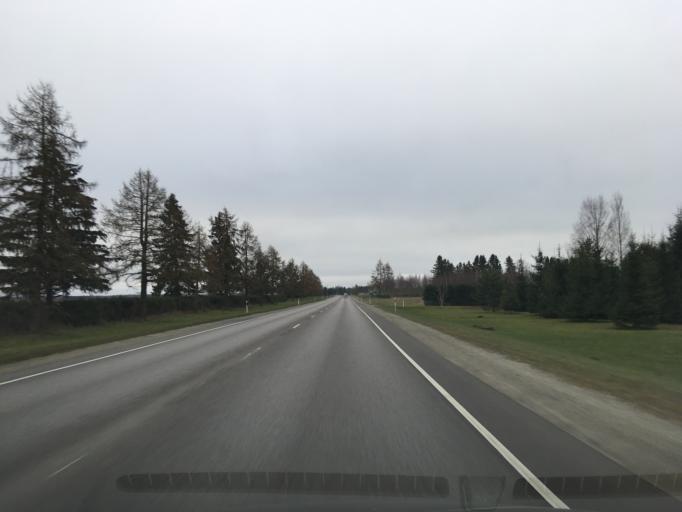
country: EE
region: Laeaene-Virumaa
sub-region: Rakvere linn
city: Rakvere
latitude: 59.4074
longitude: 26.3627
